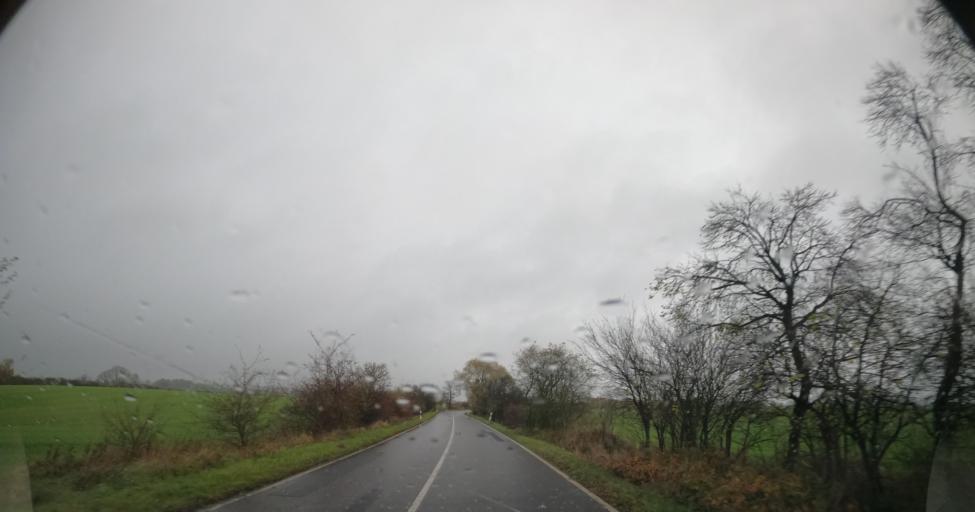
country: PL
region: West Pomeranian Voivodeship
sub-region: Powiat policki
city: Kolbaskowo
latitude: 53.3718
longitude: 14.3879
